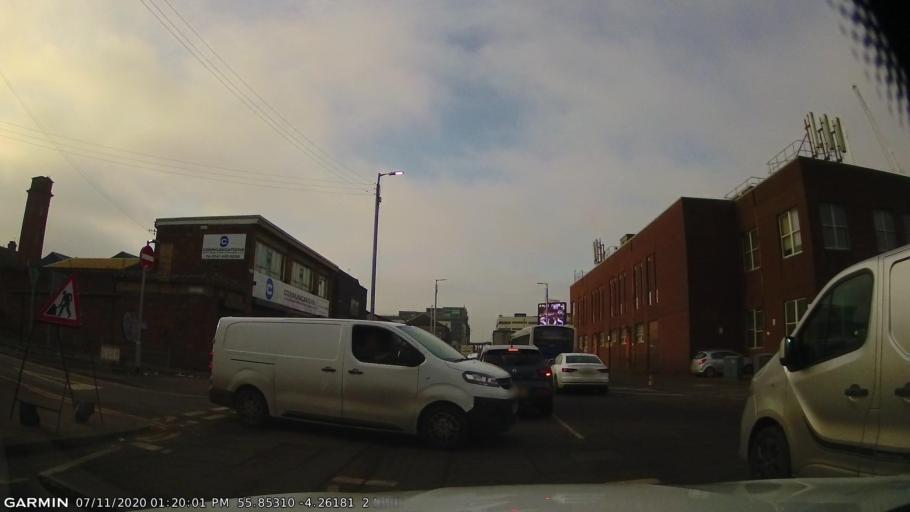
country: GB
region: Scotland
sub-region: Glasgow City
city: Glasgow
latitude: 55.8531
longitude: -4.2618
